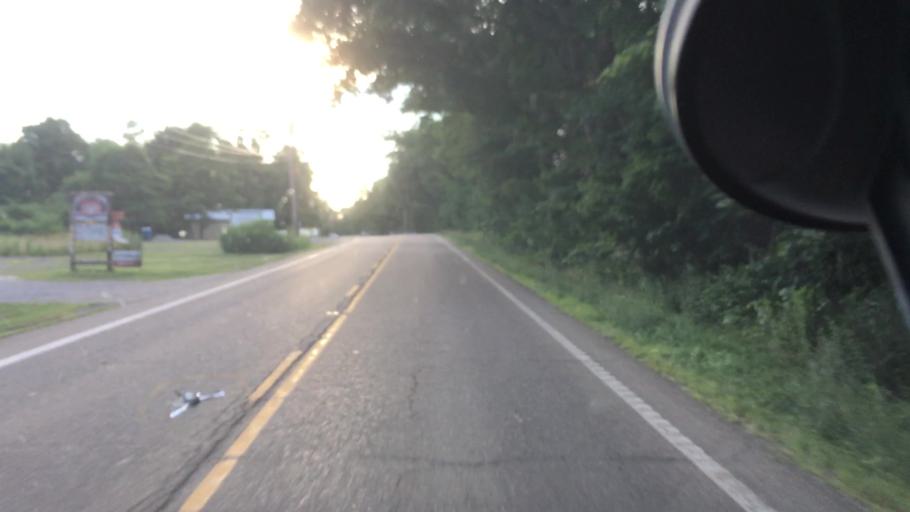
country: US
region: Ohio
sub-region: Columbiana County
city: New Waterford
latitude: 40.8782
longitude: -80.5972
